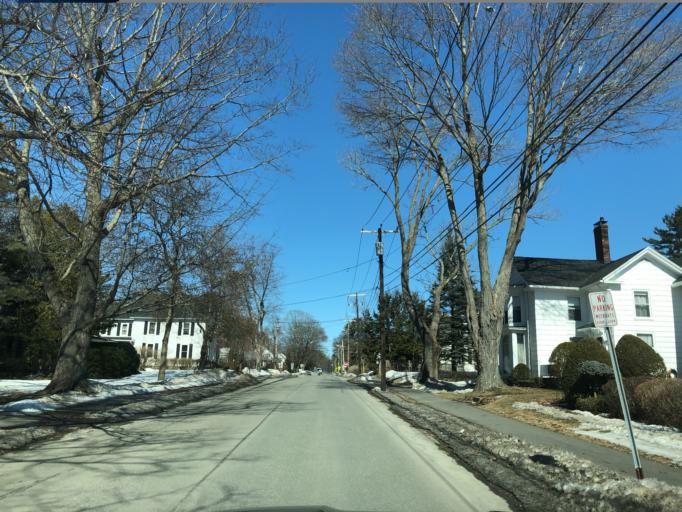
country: US
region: Maine
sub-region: Penobscot County
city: Brewer
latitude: 44.8097
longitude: -68.7521
